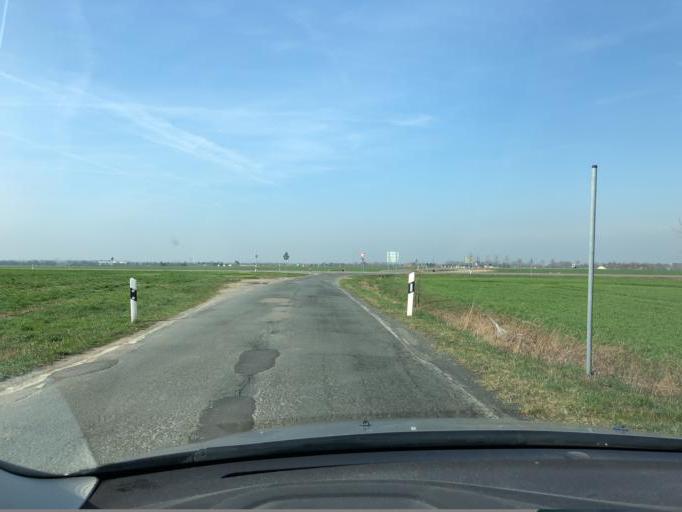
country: DE
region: Saxony
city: Rackwitz
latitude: 51.4251
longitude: 12.4048
